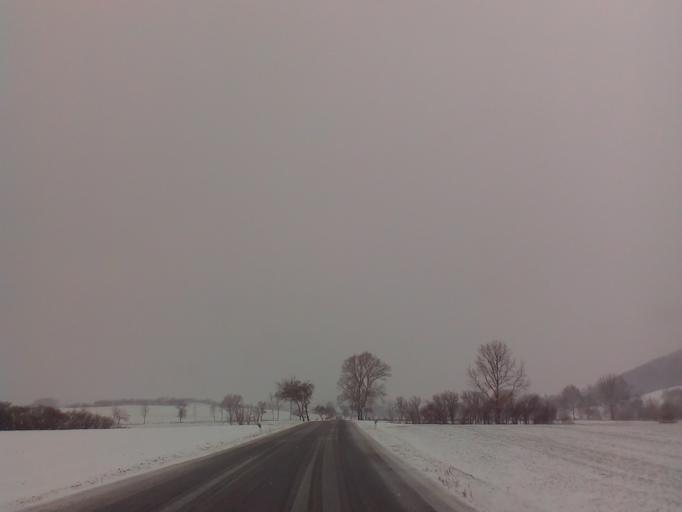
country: DE
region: Thuringia
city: Wandersleben
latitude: 50.8592
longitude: 10.8420
